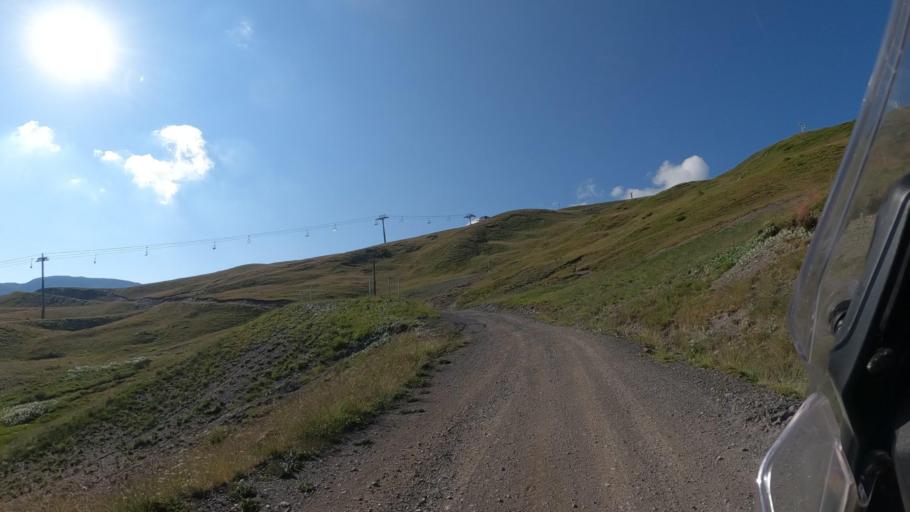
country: FR
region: Provence-Alpes-Cote d'Azur
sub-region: Departement des Hautes-Alpes
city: Guillestre
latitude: 44.6010
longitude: 6.6300
